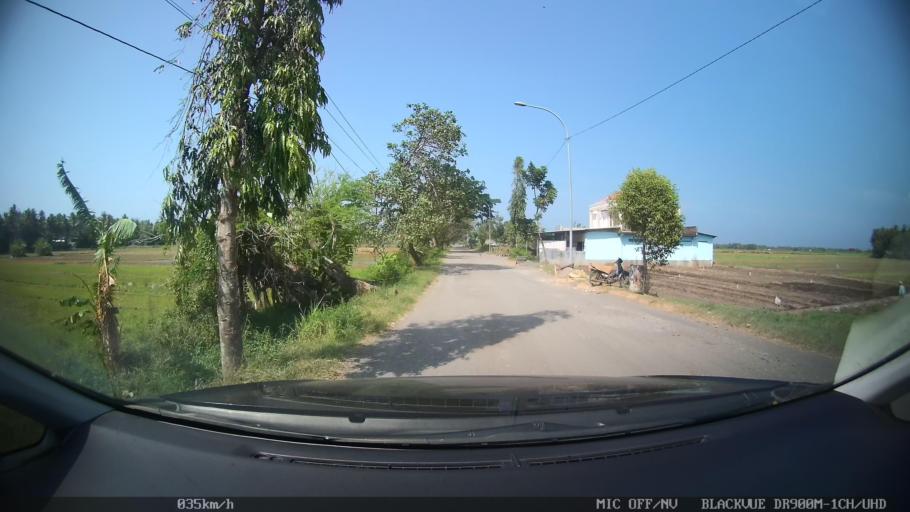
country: ID
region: Daerah Istimewa Yogyakarta
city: Srandakan
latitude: -7.9632
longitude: 110.2142
